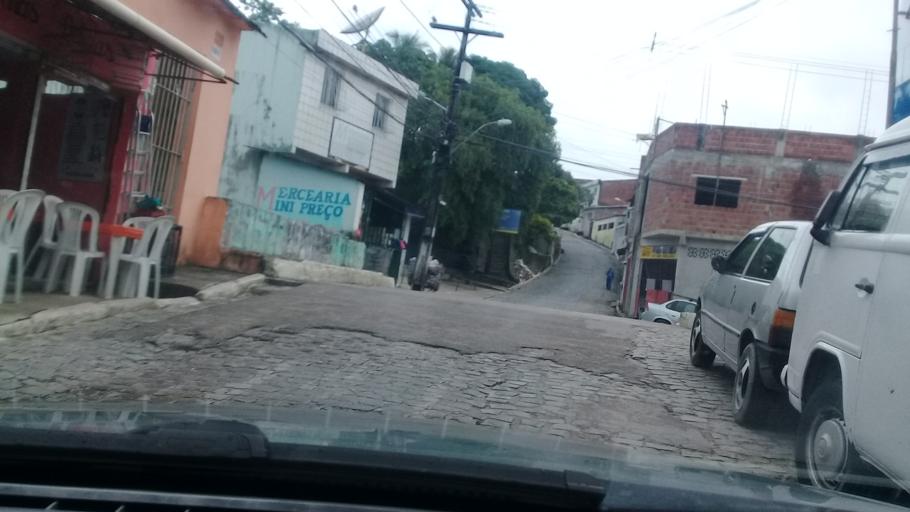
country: BR
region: Pernambuco
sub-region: Jaboatao Dos Guararapes
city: Jaboatao dos Guararapes
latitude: -8.1324
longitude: -34.9485
